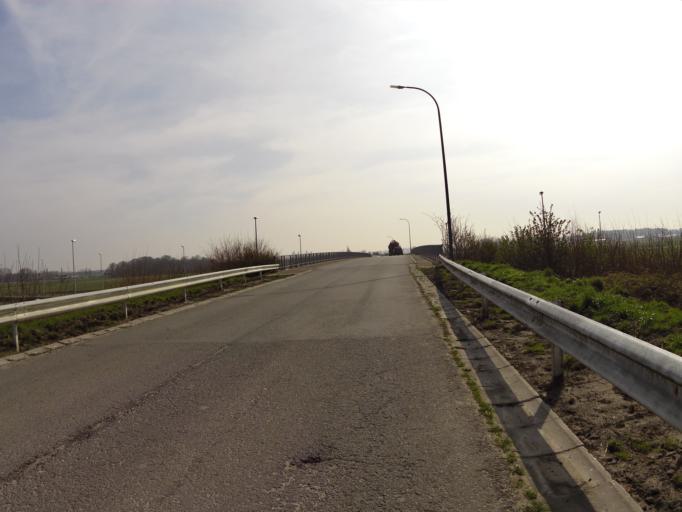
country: BE
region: Flanders
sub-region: Provincie West-Vlaanderen
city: Oudenburg
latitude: 51.1725
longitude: 2.9891
